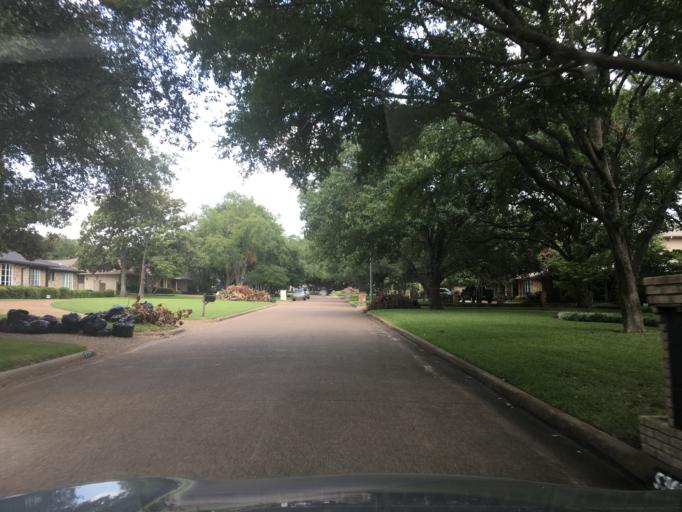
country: US
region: Texas
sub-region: Dallas County
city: University Park
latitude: 32.8971
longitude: -96.8152
